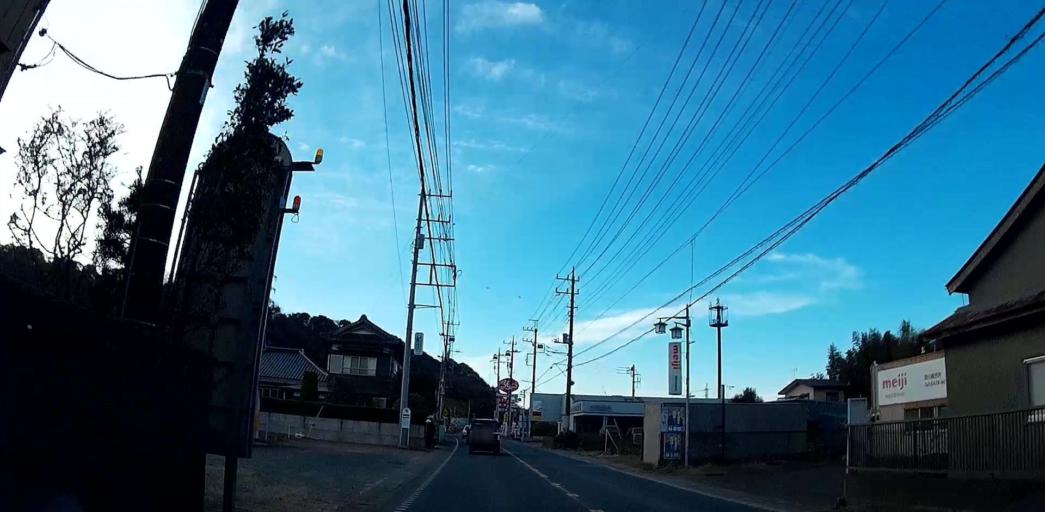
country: JP
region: Chiba
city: Omigawa
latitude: 35.8445
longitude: 140.6512
